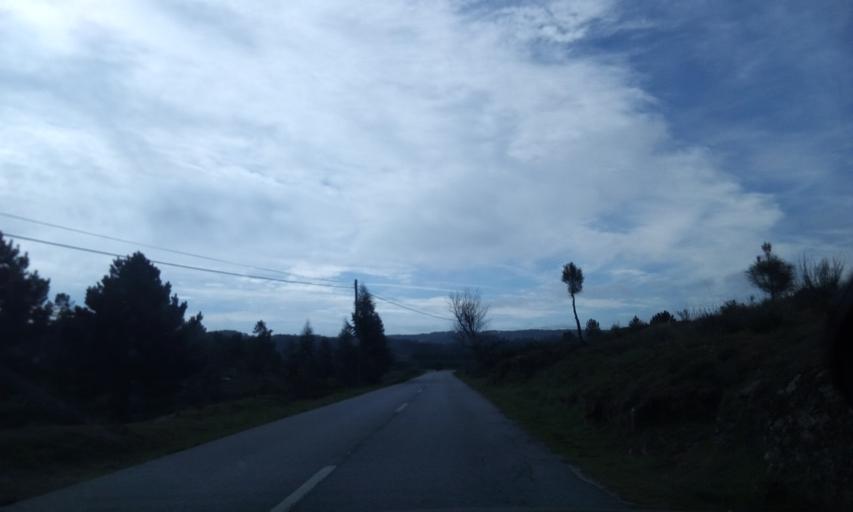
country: PT
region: Guarda
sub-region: Fornos de Algodres
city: Fornos de Algodres
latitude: 40.6731
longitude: -7.5290
